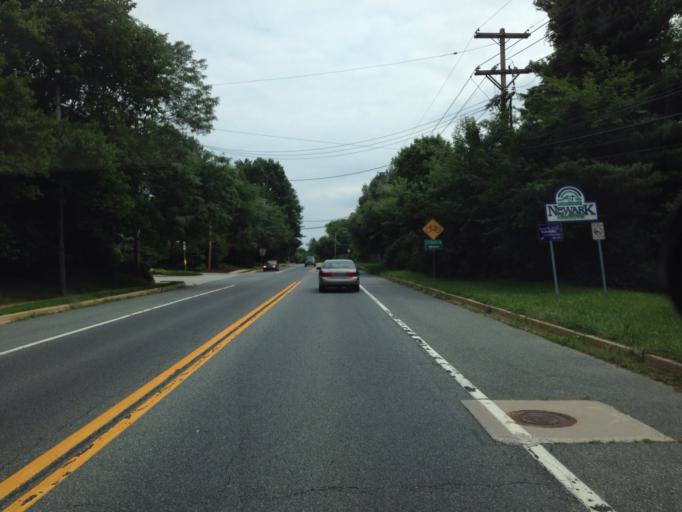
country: US
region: Delaware
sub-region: New Castle County
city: Newark
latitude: 39.7016
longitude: -75.7694
